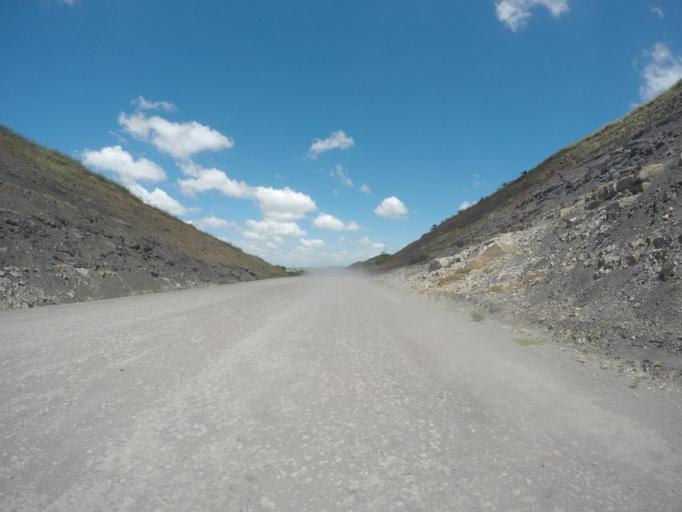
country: ZA
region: KwaZulu-Natal
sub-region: uThungulu District Municipality
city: Empangeni
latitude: -28.6288
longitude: 31.7593
